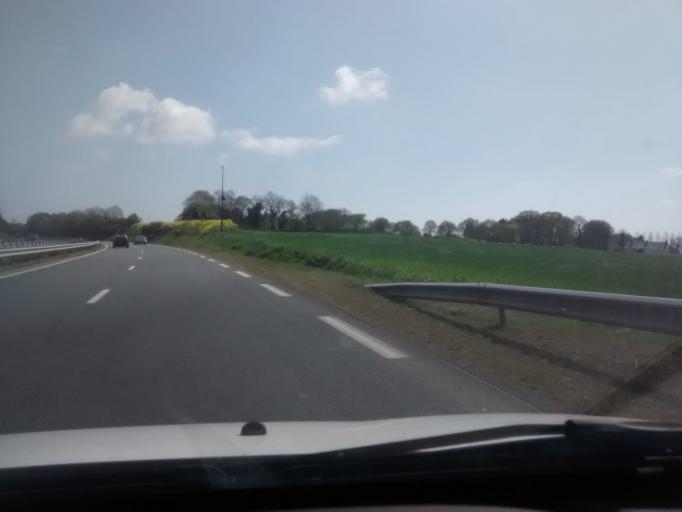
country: FR
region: Brittany
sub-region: Departement des Cotes-d'Armor
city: Begard
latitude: 48.6260
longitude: -3.3200
